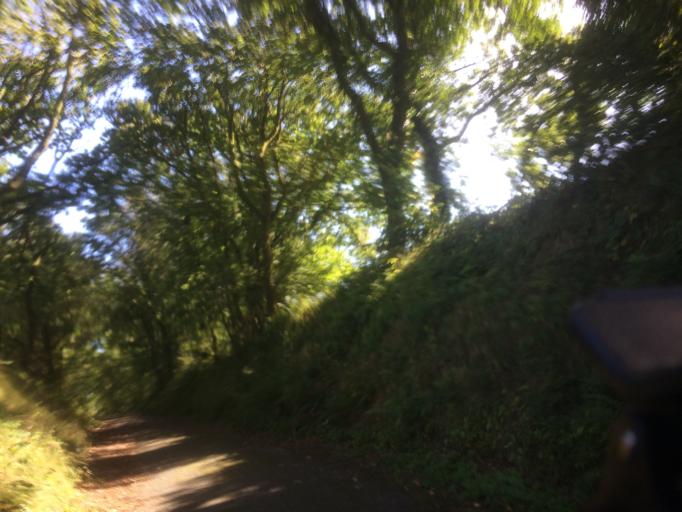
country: GB
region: England
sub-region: Devon
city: Tavistock
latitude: 50.5282
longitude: -4.1299
